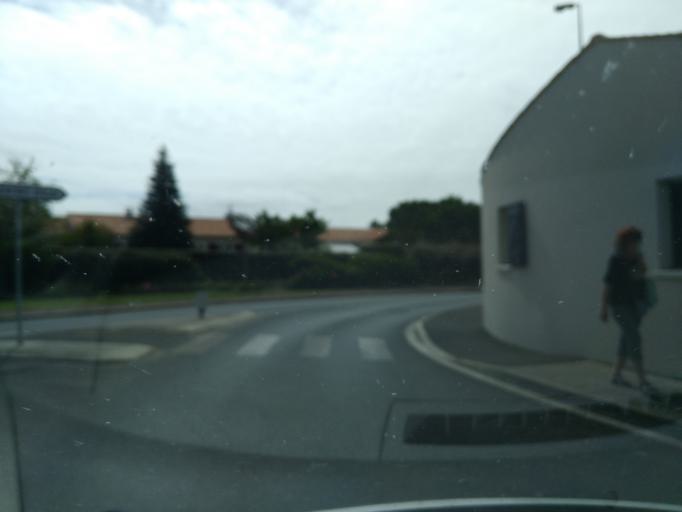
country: FR
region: Poitou-Charentes
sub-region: Departement de la Charente-Maritime
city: Saint-Palais-sur-Mer
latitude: 45.6544
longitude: -1.0842
